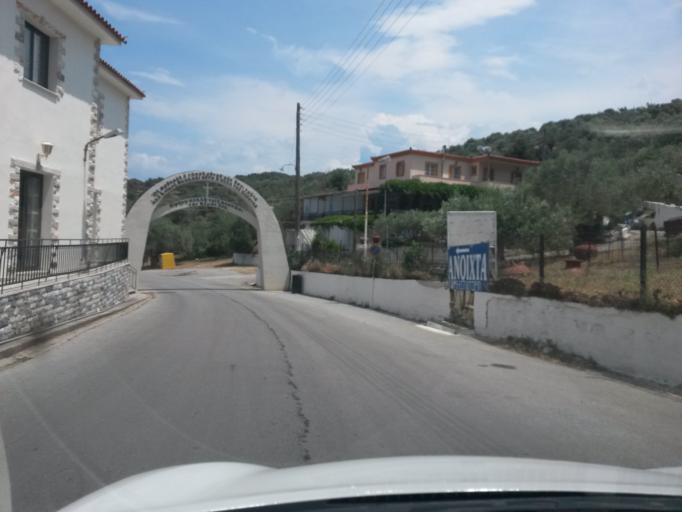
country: GR
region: North Aegean
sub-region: Nomos Lesvou
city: Pamfylla
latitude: 39.1703
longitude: 26.4825
